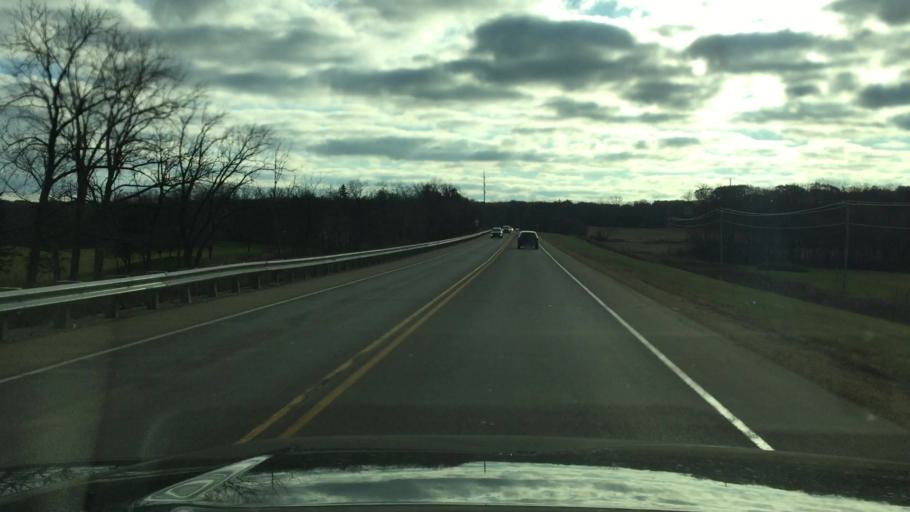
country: US
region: Wisconsin
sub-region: Walworth County
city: Williams Bay
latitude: 42.5861
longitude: -88.5285
